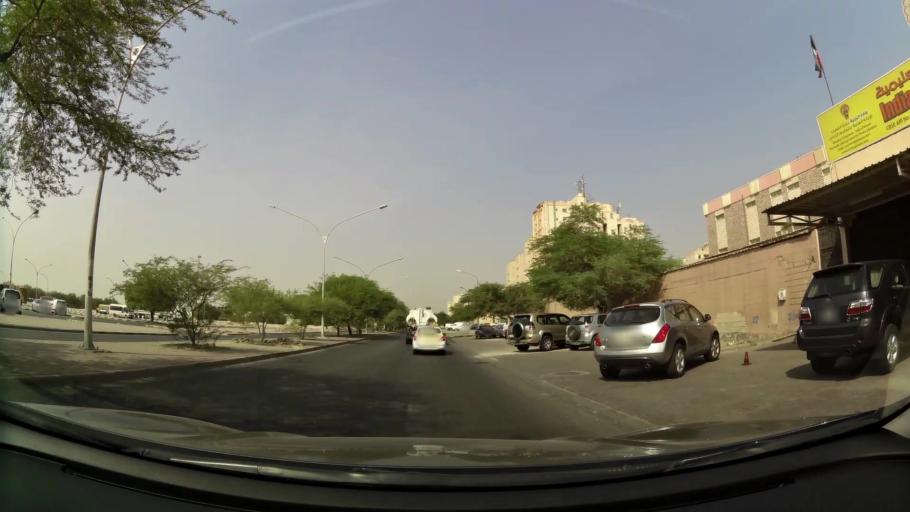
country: KW
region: Al Farwaniyah
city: Al Farwaniyah
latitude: 29.2517
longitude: 47.9280
